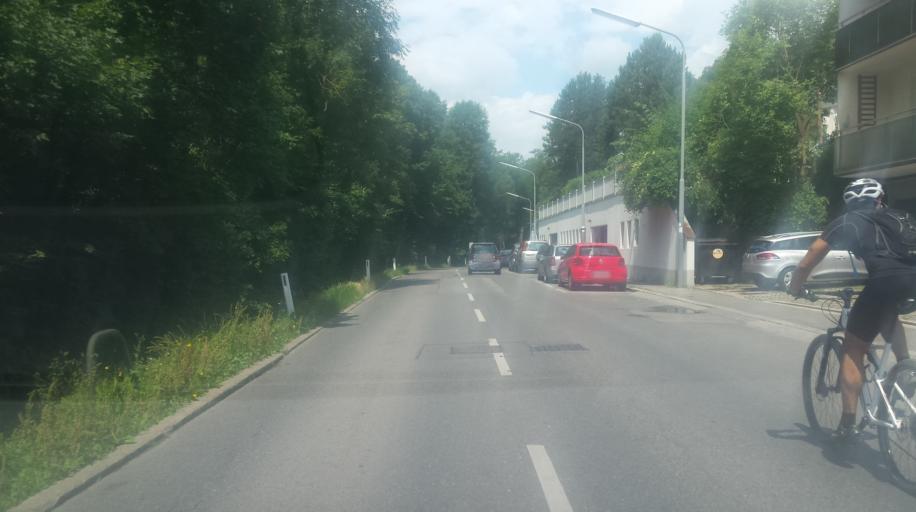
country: AT
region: Lower Austria
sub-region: Politischer Bezirk Wien-Umgebung
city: Purkersdorf
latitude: 48.2154
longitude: 16.2208
